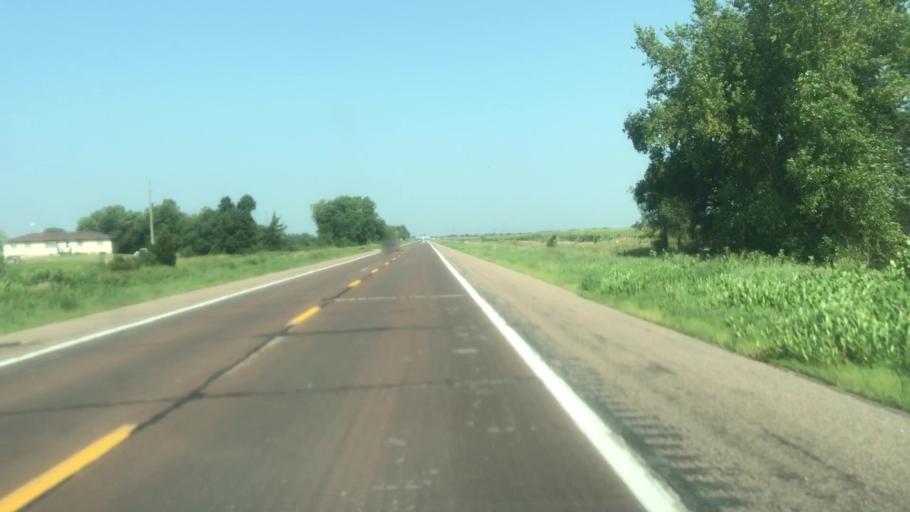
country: US
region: Nebraska
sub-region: Hall County
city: Grand Island
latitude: 40.9707
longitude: -98.5040
